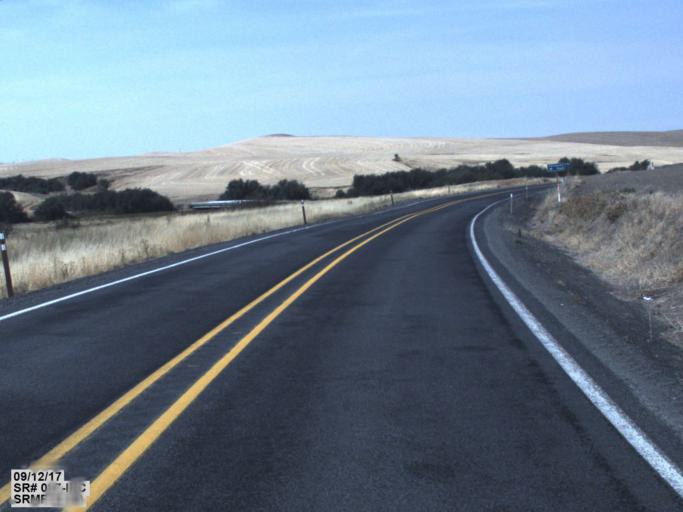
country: US
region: Idaho
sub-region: Benewah County
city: Plummer
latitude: 47.2408
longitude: -117.1284
